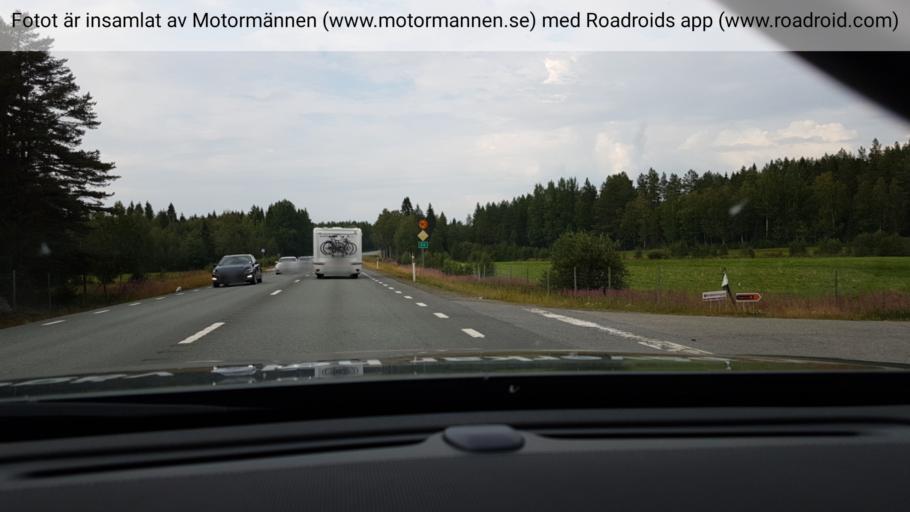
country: SE
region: Vaesterbotten
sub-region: Robertsfors Kommun
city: Robertsfors
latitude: 64.0314
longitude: 20.8417
